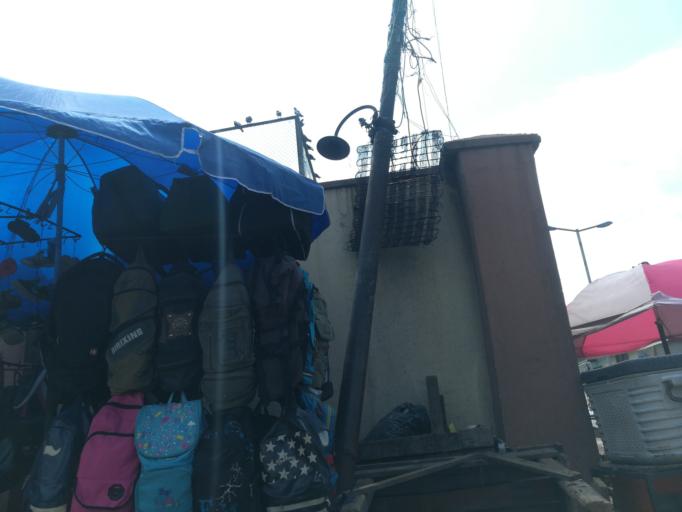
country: NG
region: Lagos
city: Lagos
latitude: 6.4516
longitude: 3.3953
